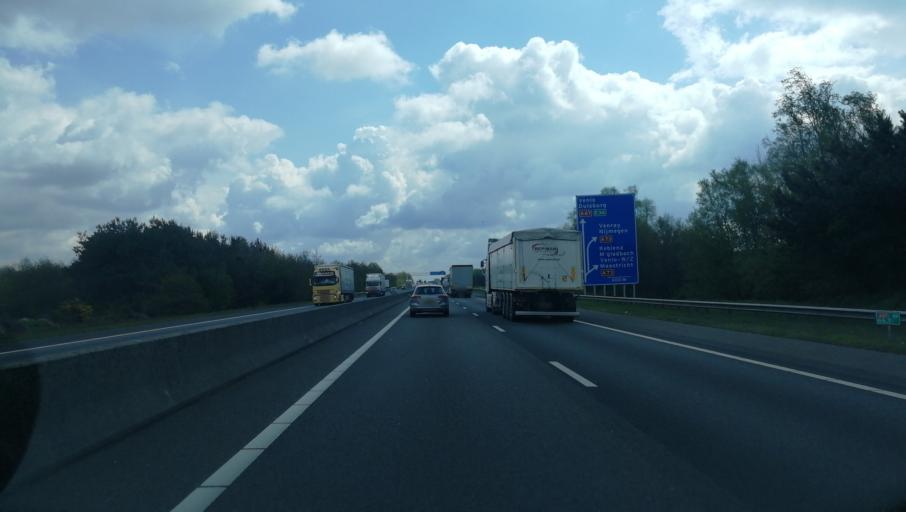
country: NL
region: Limburg
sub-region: Gemeente Venlo
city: Tegelen
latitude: 51.3949
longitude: 6.0991
